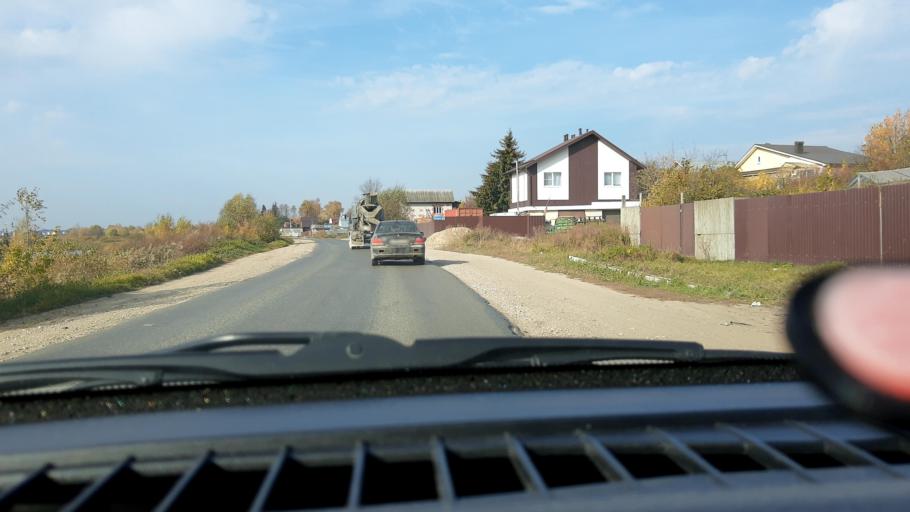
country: RU
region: Nizjnij Novgorod
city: Neklyudovo
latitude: 56.4174
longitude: 43.9691
